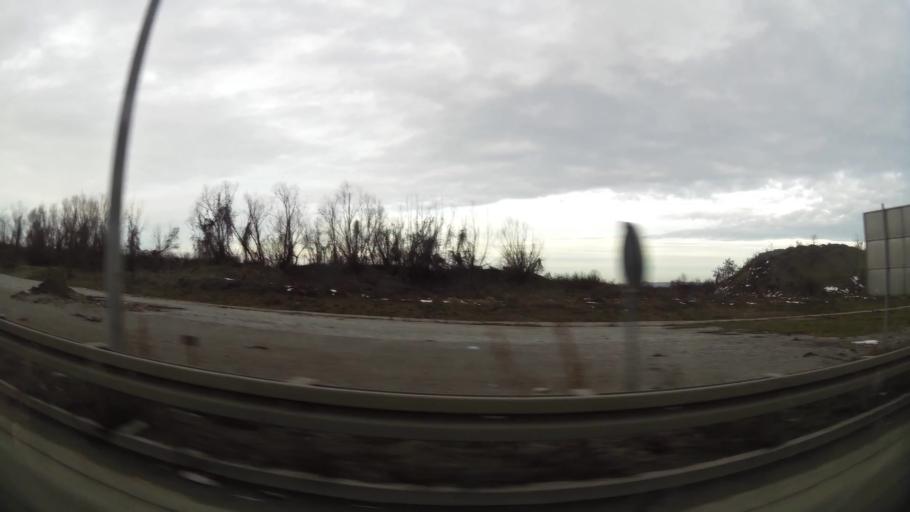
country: RS
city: Ostruznica
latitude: 44.7309
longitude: 20.3407
